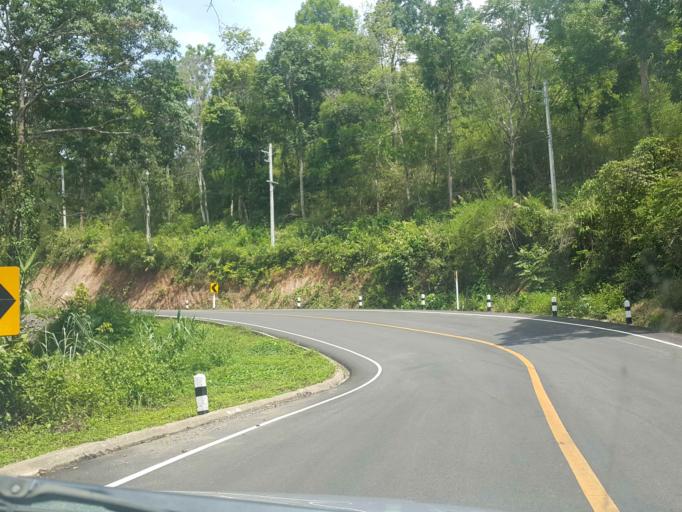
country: TH
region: Nan
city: Ban Luang
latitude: 18.8730
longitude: 100.5184
